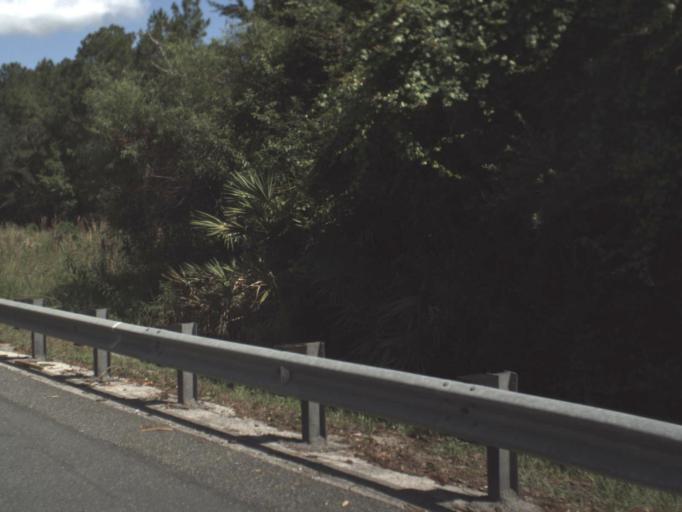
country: US
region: Florida
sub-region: Putnam County
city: Palatka
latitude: 29.6683
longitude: -81.6989
